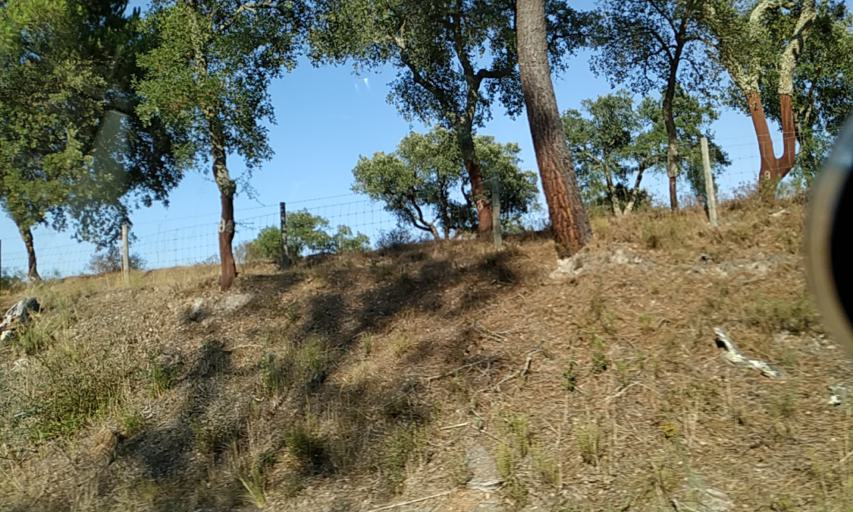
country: PT
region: Santarem
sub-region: Coruche
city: Coruche
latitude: 39.0543
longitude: -8.5669
